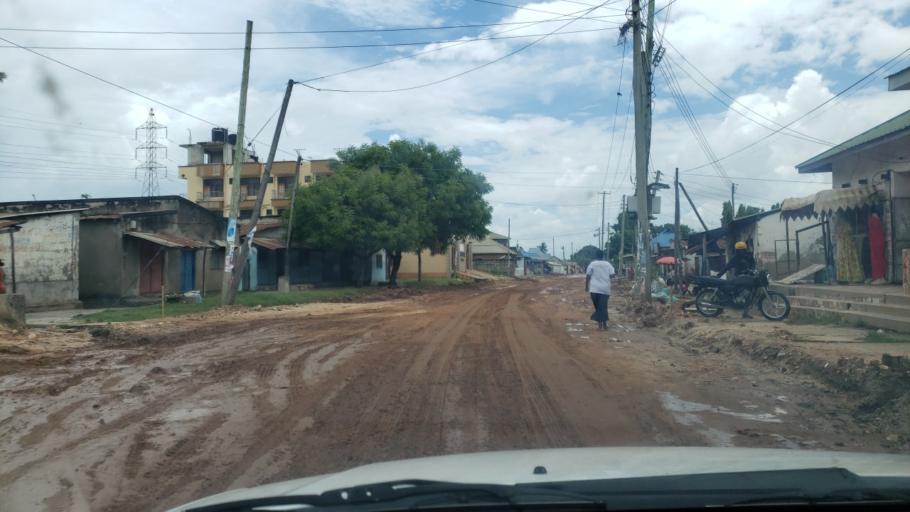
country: TZ
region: Dar es Salaam
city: Magomeni
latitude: -6.8076
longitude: 39.2352
